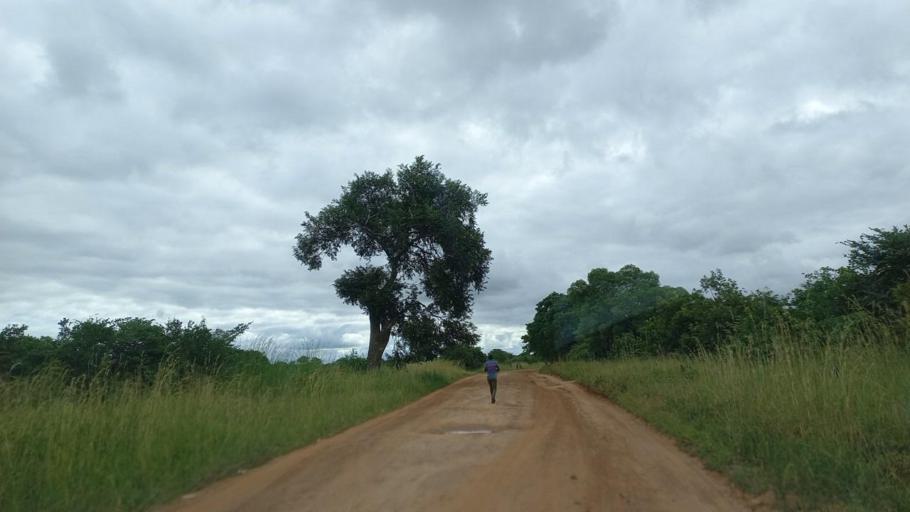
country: ZM
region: Lusaka
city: Chongwe
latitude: -15.4569
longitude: 28.8781
